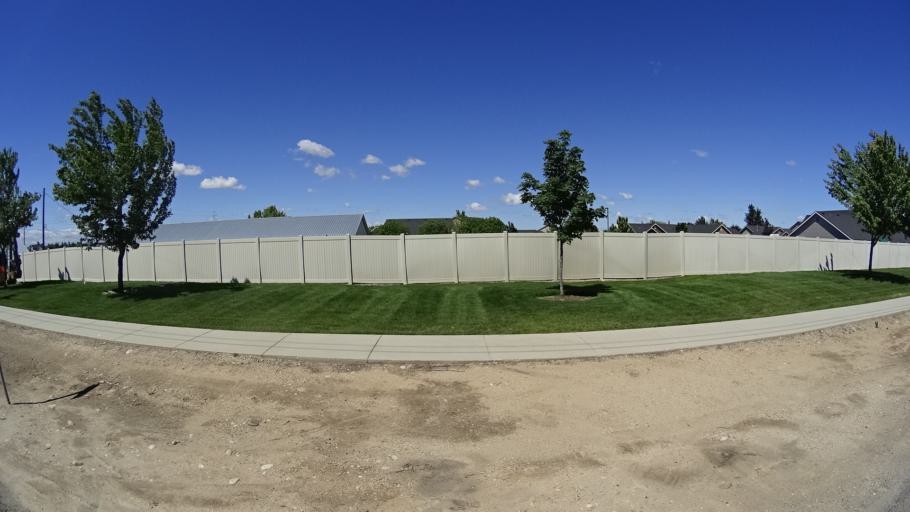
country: US
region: Idaho
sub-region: Ada County
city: Meridian
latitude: 43.6502
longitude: -116.3746
